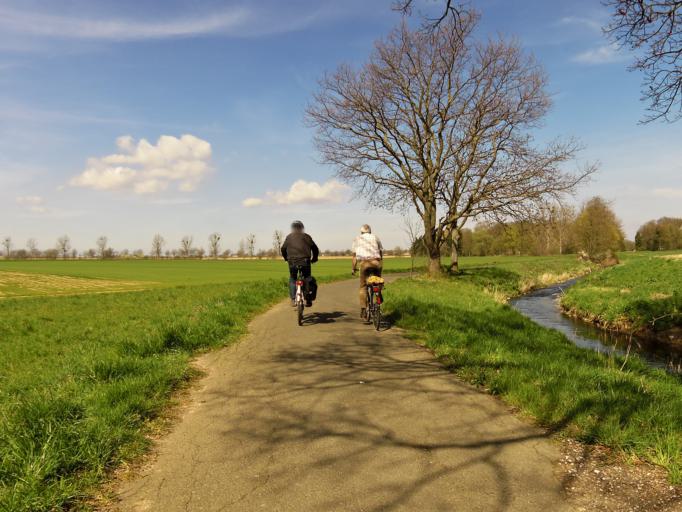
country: DE
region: North Rhine-Westphalia
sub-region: Regierungsbezirk Koln
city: Rheinbach
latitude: 50.7021
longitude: 6.9225
